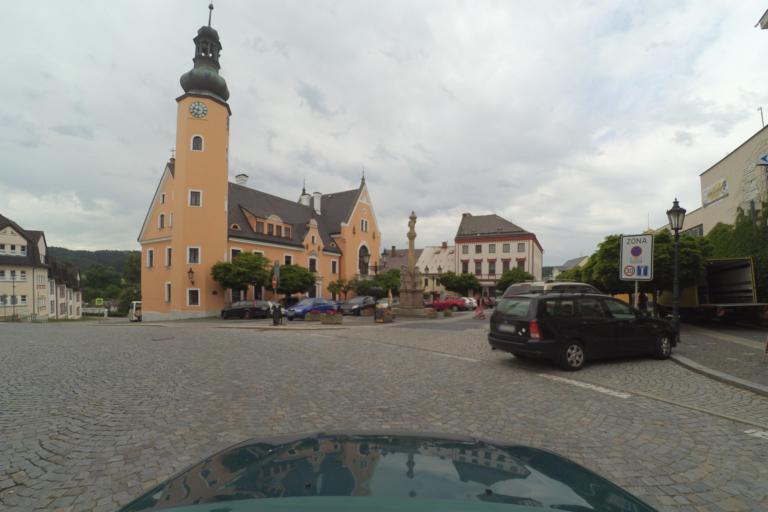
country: CZ
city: Cesky Dub
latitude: 50.6611
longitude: 14.9961
